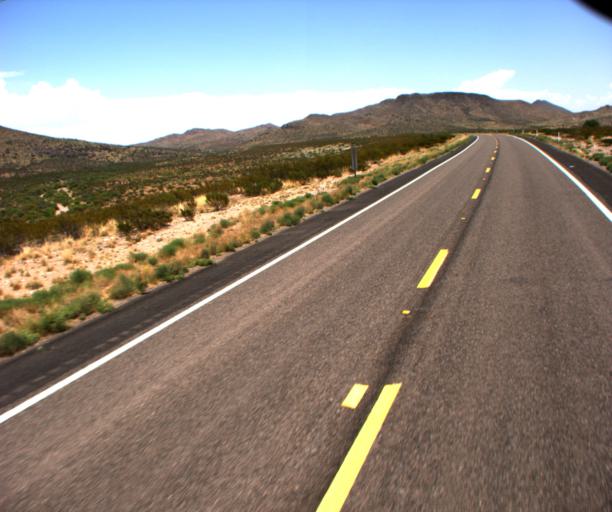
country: US
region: Arizona
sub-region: Greenlee County
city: Clifton
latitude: 32.7517
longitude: -109.3465
